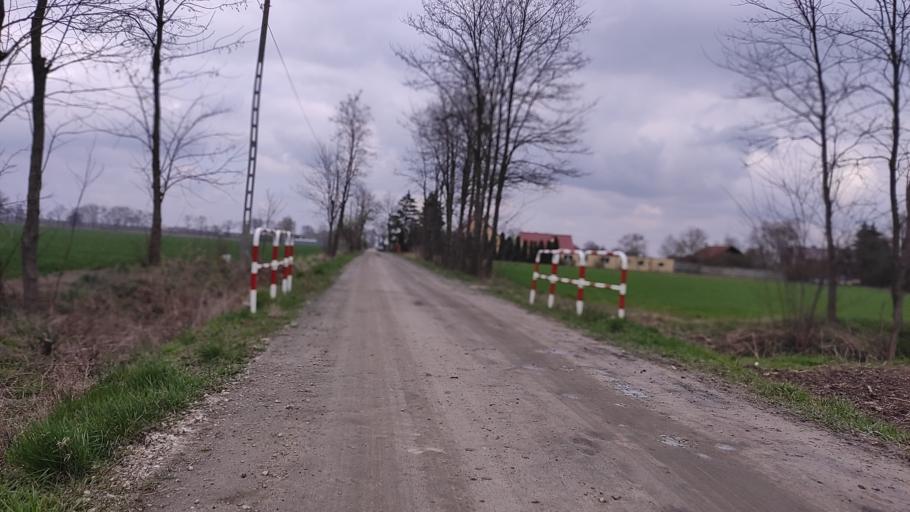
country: PL
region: Greater Poland Voivodeship
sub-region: Powiat poznanski
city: Swarzedz
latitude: 52.4074
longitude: 17.1390
